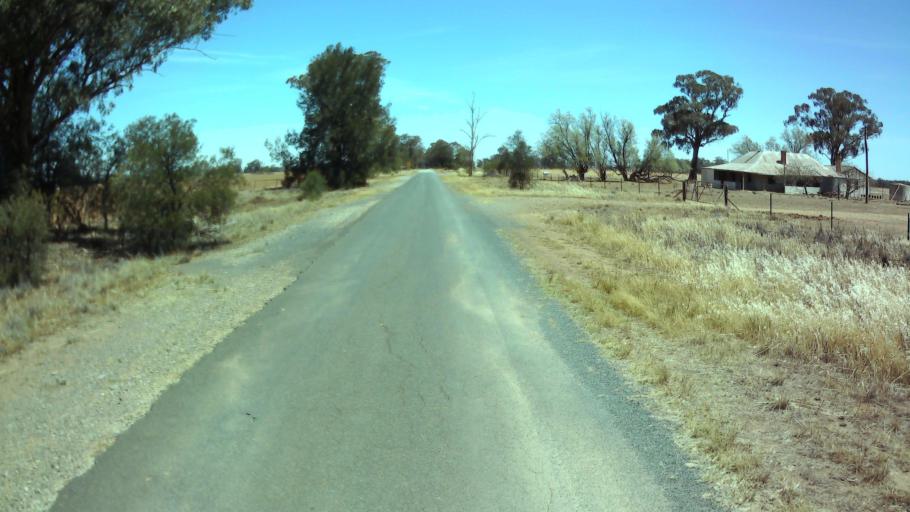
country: AU
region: New South Wales
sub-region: Weddin
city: Grenfell
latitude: -33.9051
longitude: 147.6856
